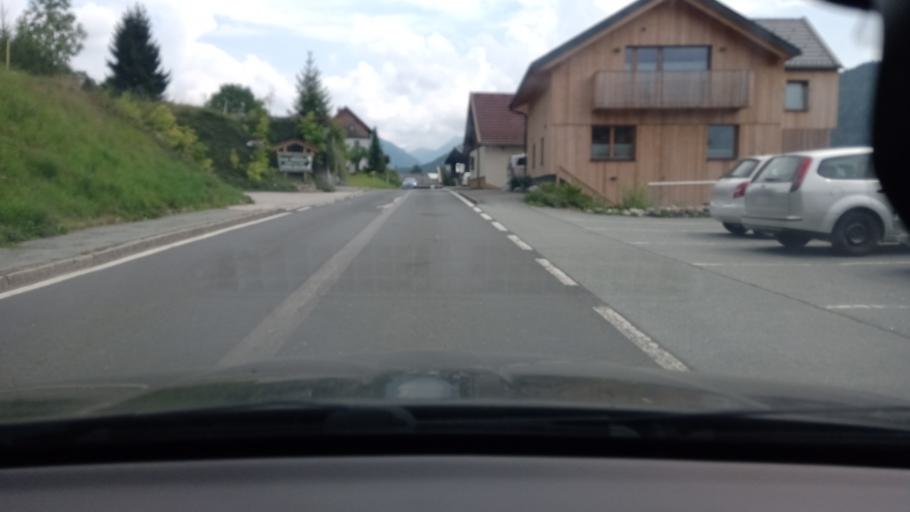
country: AT
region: Carinthia
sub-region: Politischer Bezirk Spittal an der Drau
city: Steinfeld
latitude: 46.7194
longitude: 13.2845
